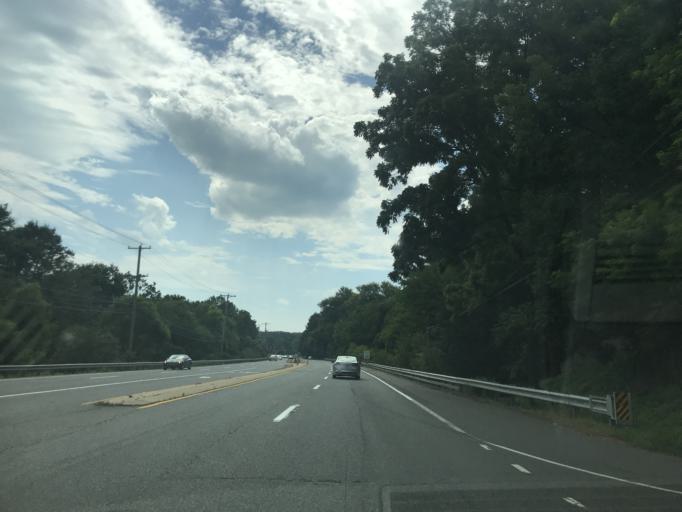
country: US
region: Pennsylvania
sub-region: Chester County
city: West Chester
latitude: 39.8735
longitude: -75.5840
